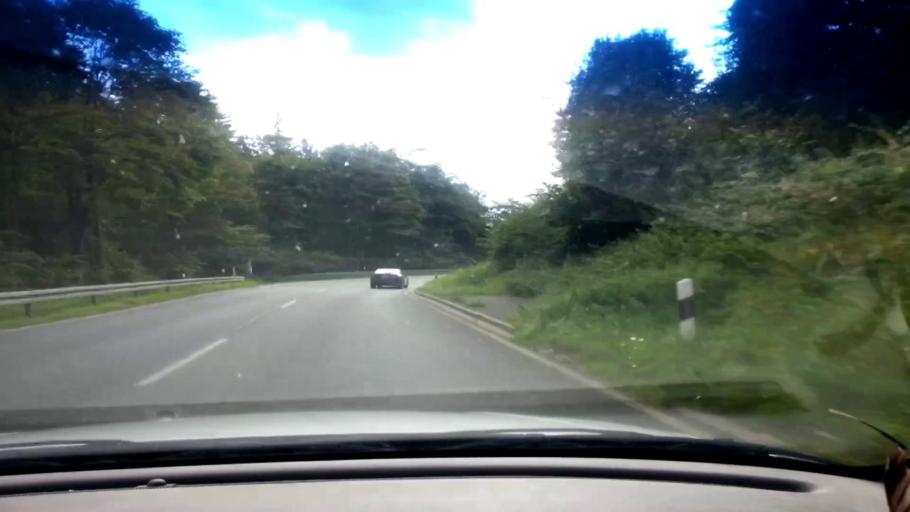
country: DE
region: Bavaria
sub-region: Upper Franconia
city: Goldkronach
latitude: 50.0349
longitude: 11.7112
